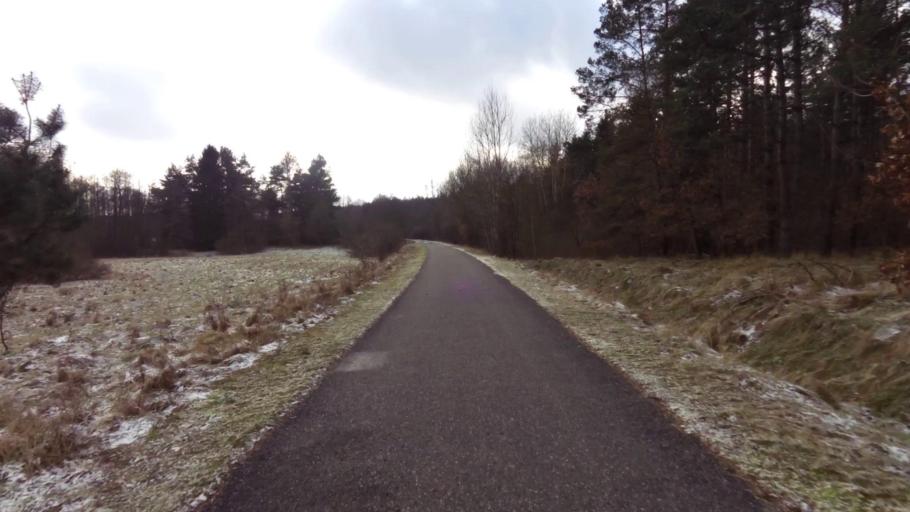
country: PL
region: West Pomeranian Voivodeship
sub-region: Powiat drawski
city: Zlocieniec
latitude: 53.5823
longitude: 16.0421
